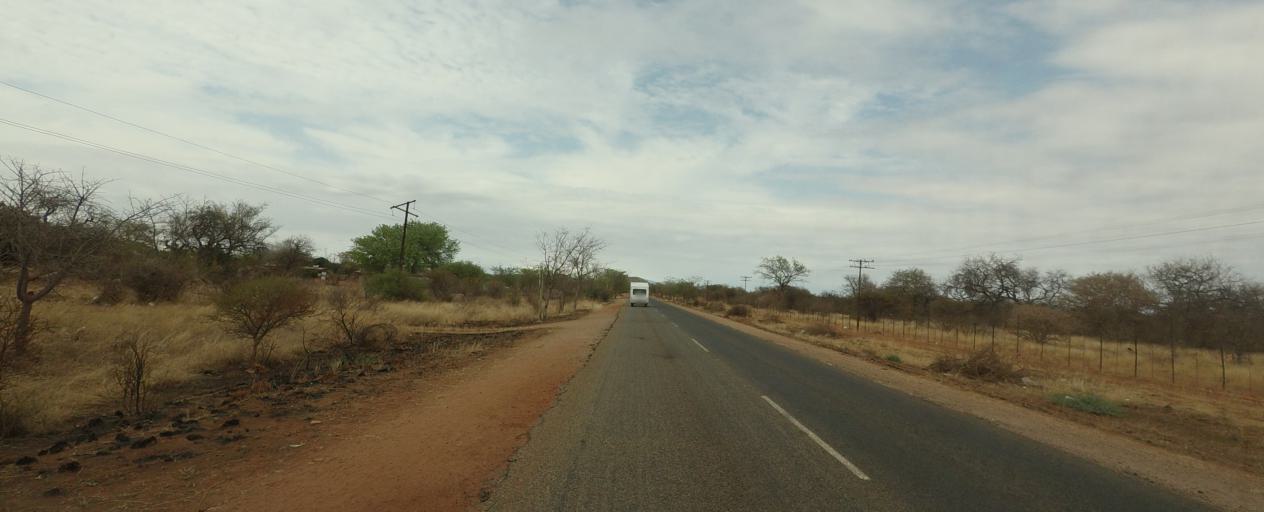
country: BW
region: Central
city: Mathathane
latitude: -22.6589
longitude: 29.1146
